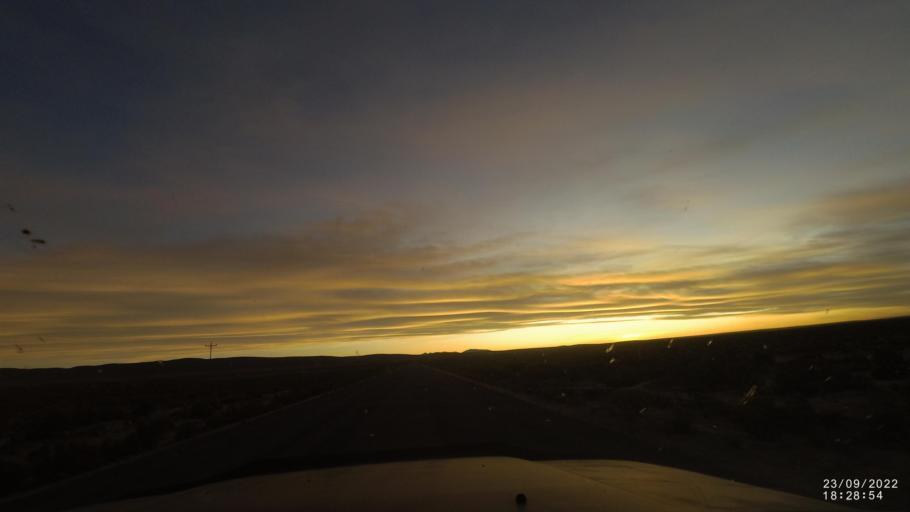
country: BO
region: Oruro
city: Challapata
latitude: -19.3411
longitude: -67.1843
